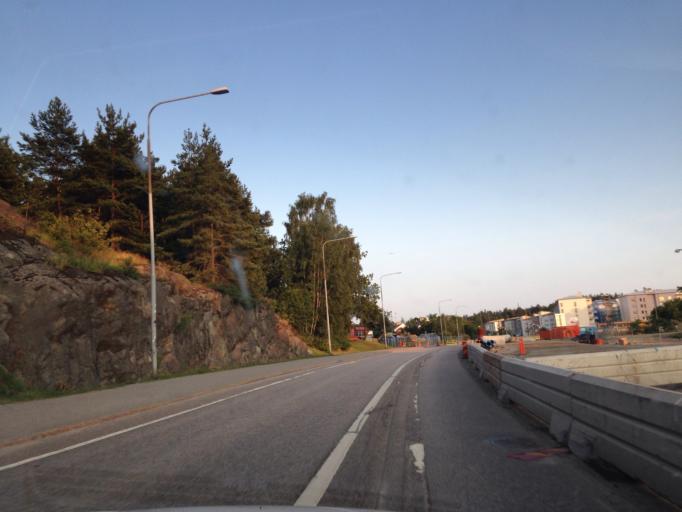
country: SE
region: Stockholm
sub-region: Varmdo Kommun
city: Gustavsberg
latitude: 59.3231
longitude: 18.3864
